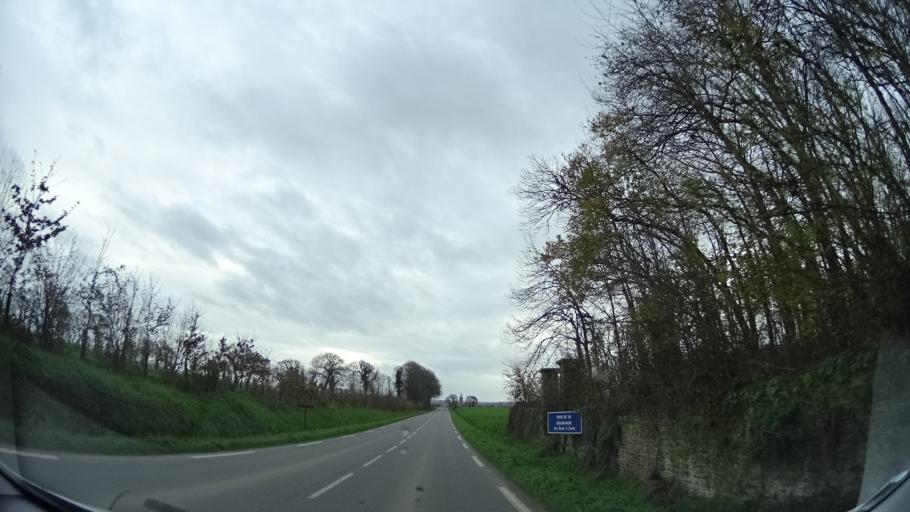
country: FR
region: Brittany
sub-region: Departement des Cotes-d'Armor
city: Evran
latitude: 48.3941
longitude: -1.9800
